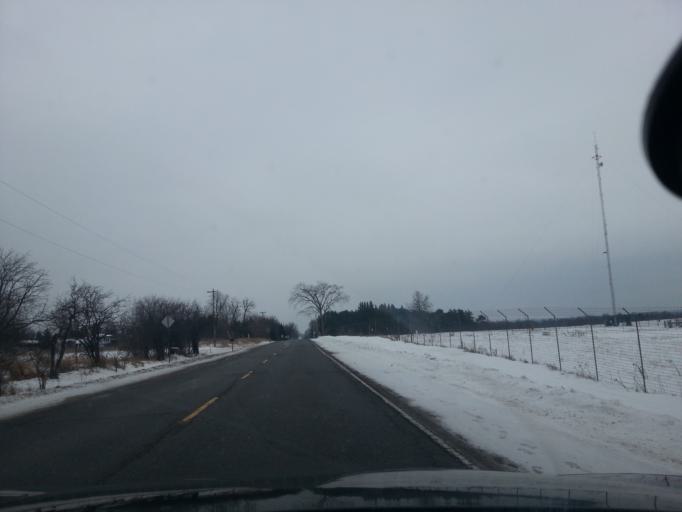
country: CA
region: Ontario
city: Bells Corners
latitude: 45.3543
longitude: -76.0479
